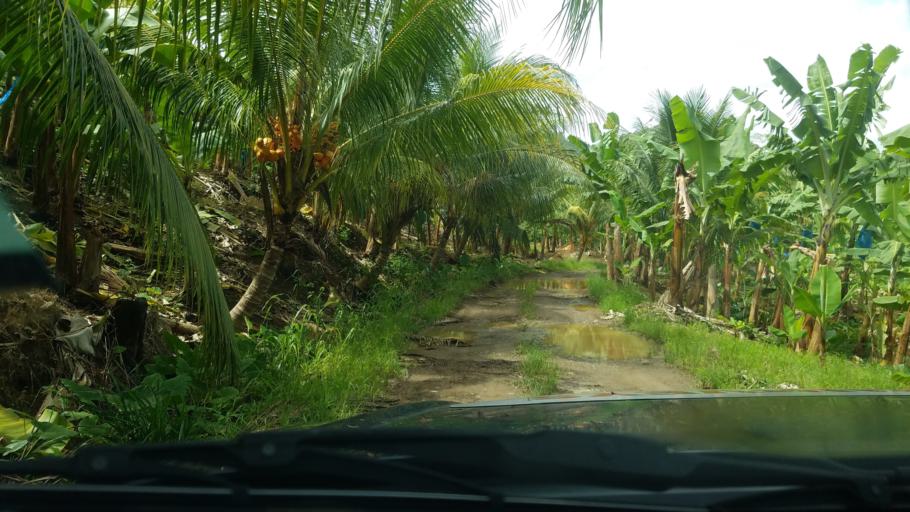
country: LC
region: Anse-la-Raye
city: Anse La Raye
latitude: 13.9370
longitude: -60.9898
